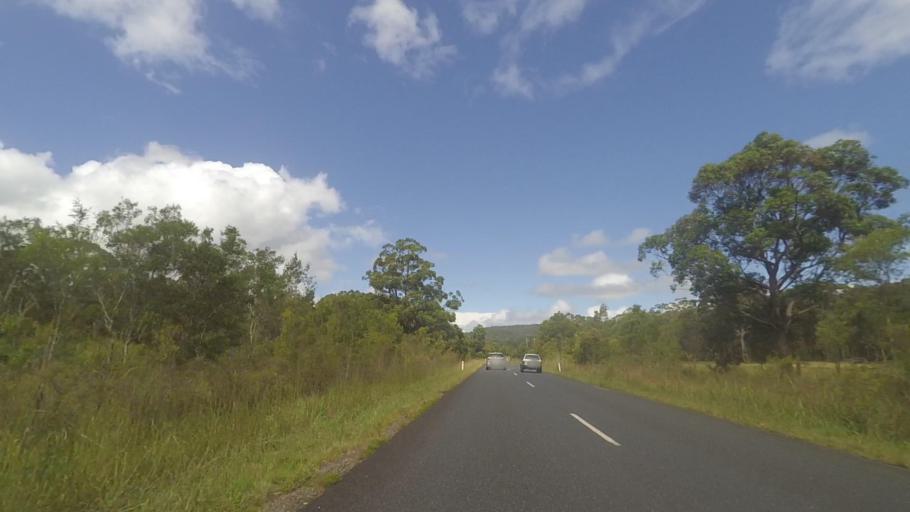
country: AU
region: New South Wales
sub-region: Great Lakes
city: Bulahdelah
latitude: -32.4020
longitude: 152.2661
